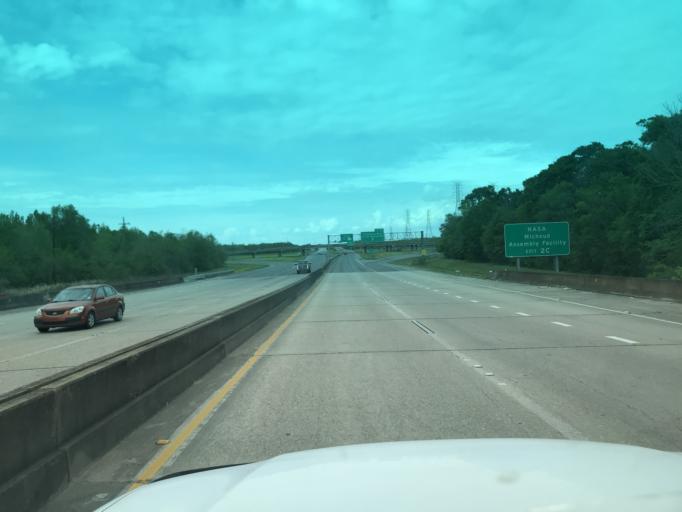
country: US
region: Louisiana
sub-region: Saint Bernard Parish
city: Chalmette
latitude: 30.0136
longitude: -89.9397
